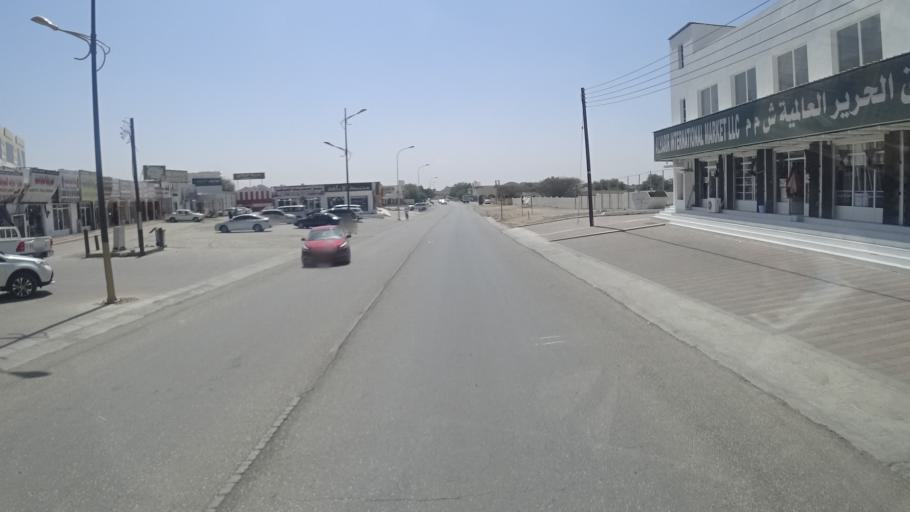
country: OM
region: Ash Sharqiyah
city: Ibra'
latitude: 22.6910
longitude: 58.5440
